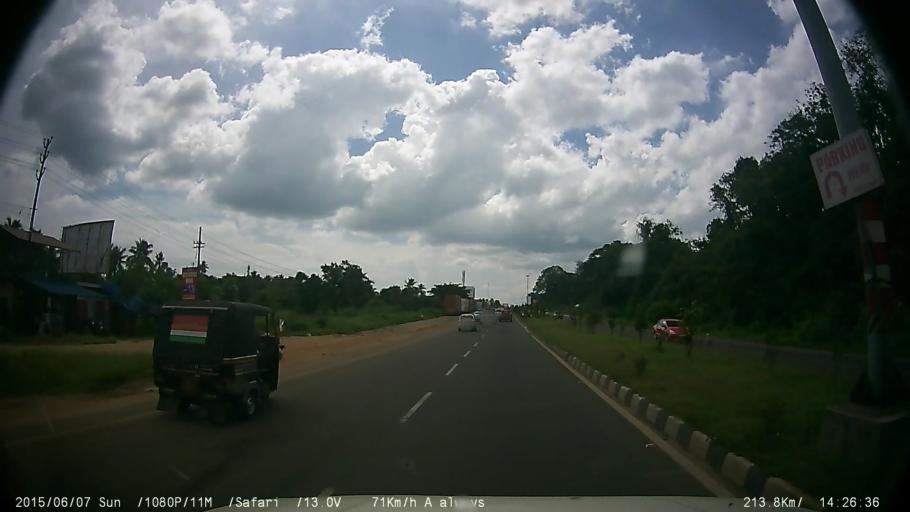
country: IN
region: Kerala
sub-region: Thrissur District
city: Kizhake Chalakudi
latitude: 10.2645
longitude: 76.3526
